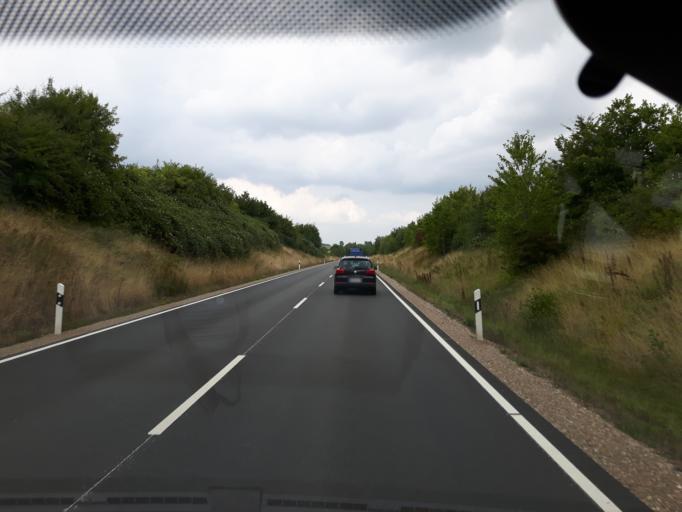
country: DE
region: Schleswig-Holstein
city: Gross Wittensee
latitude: 54.4084
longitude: 9.7611
